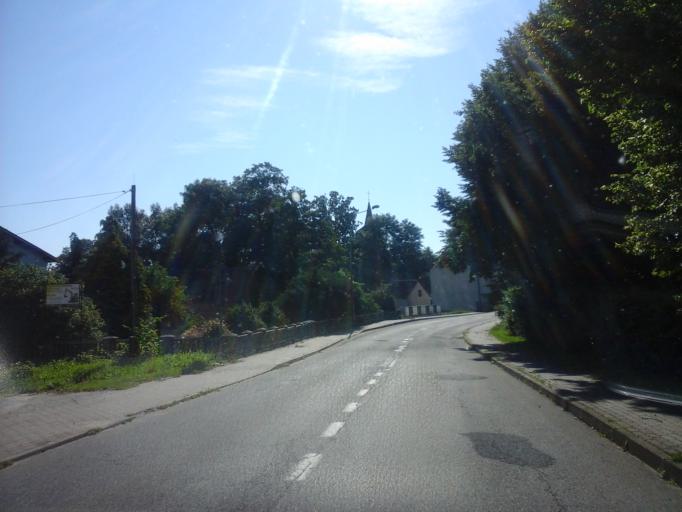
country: PL
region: West Pomeranian Voivodeship
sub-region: Powiat drawski
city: Zlocieniec
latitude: 53.6386
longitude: 15.9714
